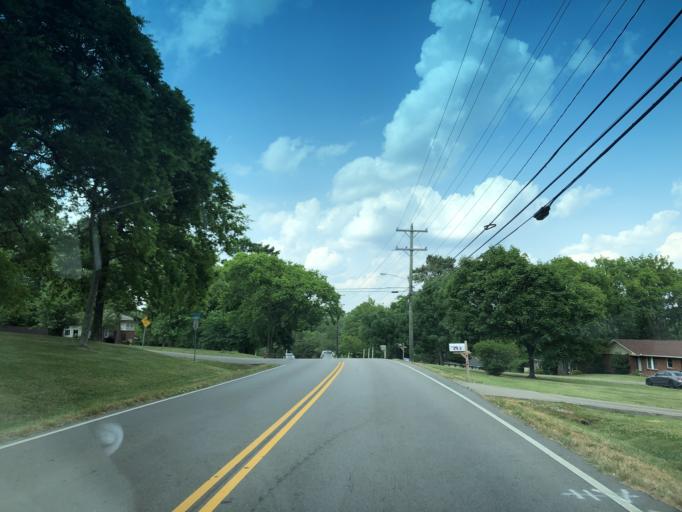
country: US
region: Tennessee
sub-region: Davidson County
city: Goodlettsville
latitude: 36.2680
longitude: -86.7305
